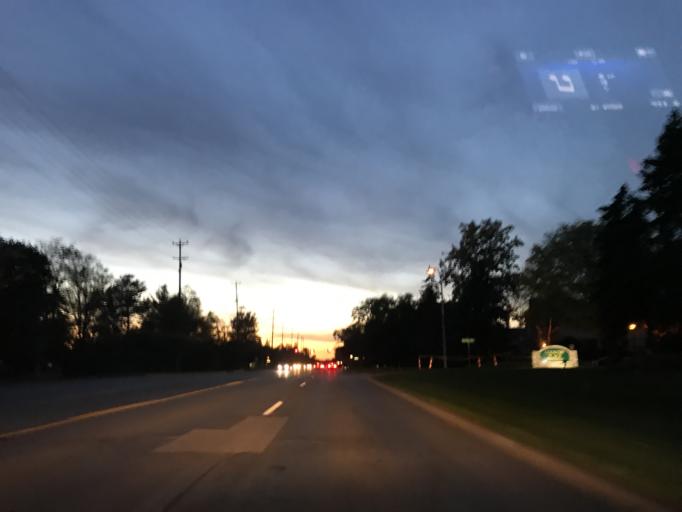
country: US
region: Michigan
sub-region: Wayne County
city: Northville
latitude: 42.4383
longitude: -83.4575
